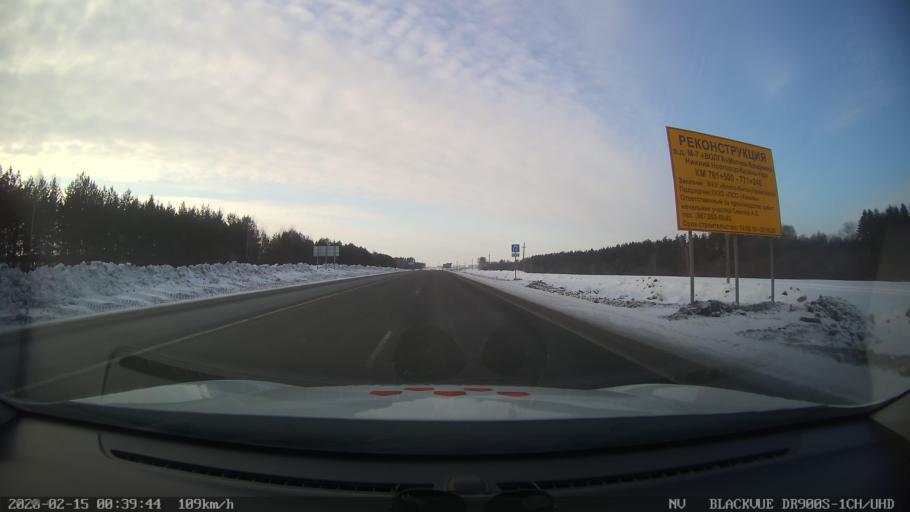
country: RU
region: Tatarstan
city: Sviyazhsk
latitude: 55.7316
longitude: 48.8013
